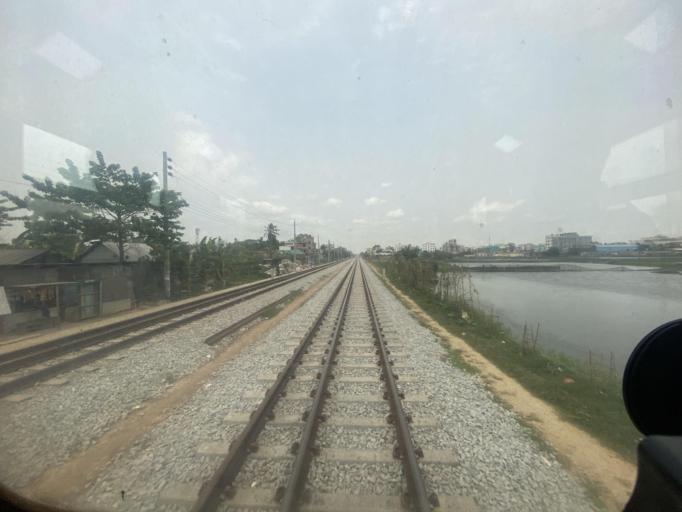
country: BD
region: Chittagong
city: Comilla
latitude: 23.4518
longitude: 91.1692
